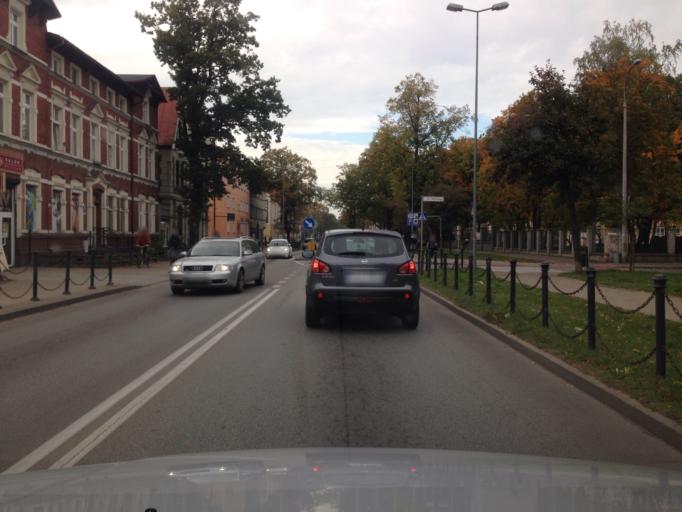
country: PL
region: Pomeranian Voivodeship
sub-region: Powiat leborski
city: Lebork
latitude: 54.5368
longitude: 17.7518
